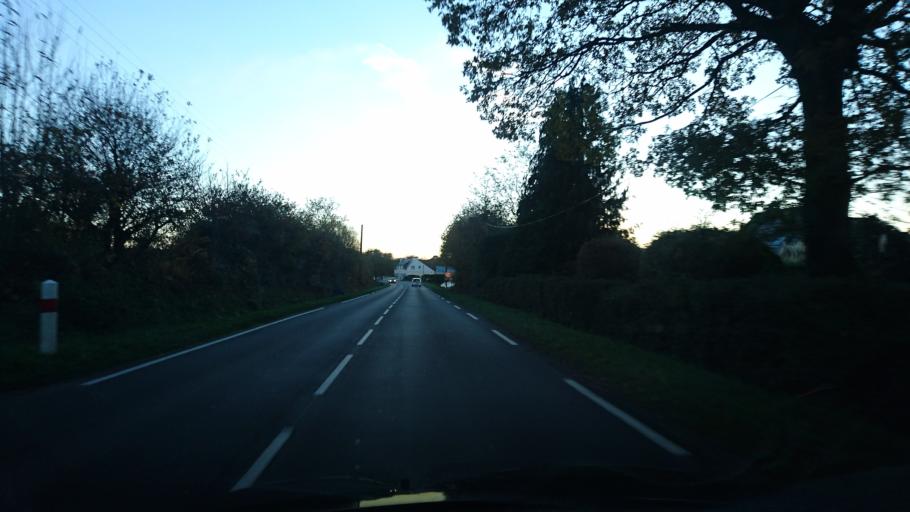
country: FR
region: Brittany
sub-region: Departement du Finistere
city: Quimperle
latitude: 47.8558
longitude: -3.5676
